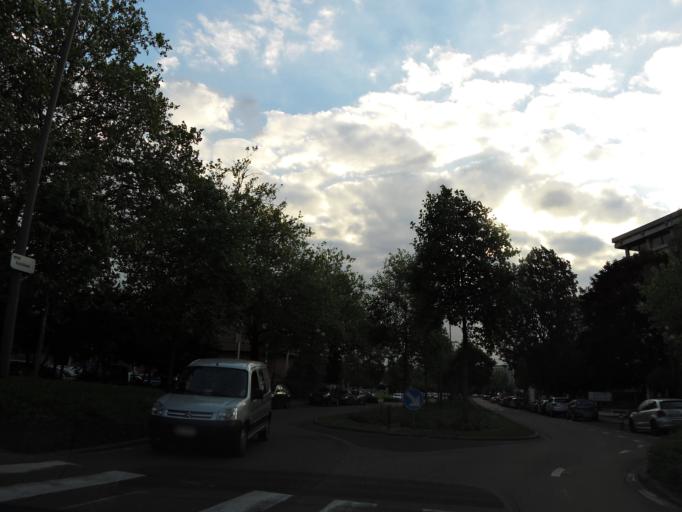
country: BE
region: Flanders
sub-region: Provincie Limburg
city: Hasselt
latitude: 50.9266
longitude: 5.3487
